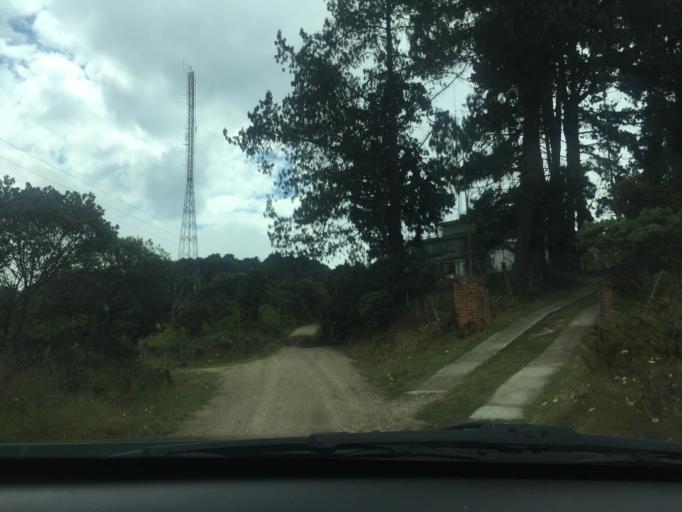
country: CO
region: Cundinamarca
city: Facatativa
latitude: 4.8023
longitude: -74.3895
